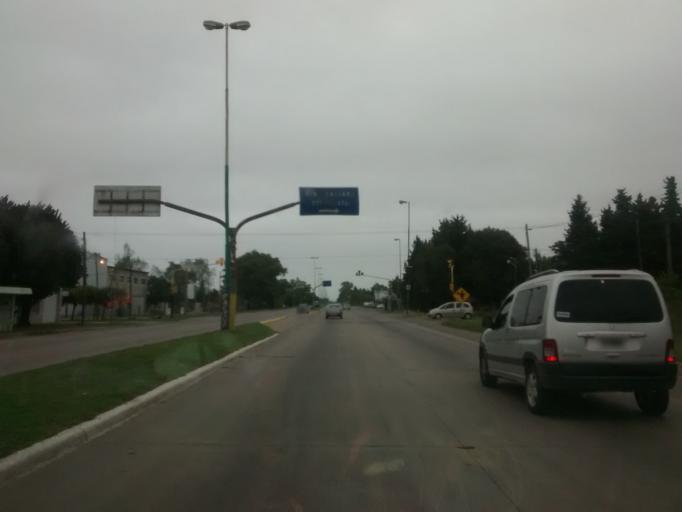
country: AR
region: Buenos Aires
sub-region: Partido de La Plata
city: La Plata
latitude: -35.0053
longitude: -58.0594
